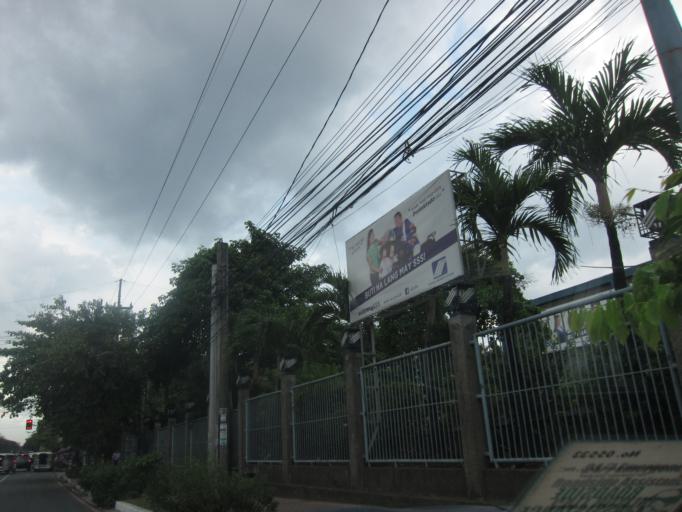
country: PH
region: Metro Manila
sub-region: Quezon City
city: Quezon City
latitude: 14.6402
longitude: 121.0468
